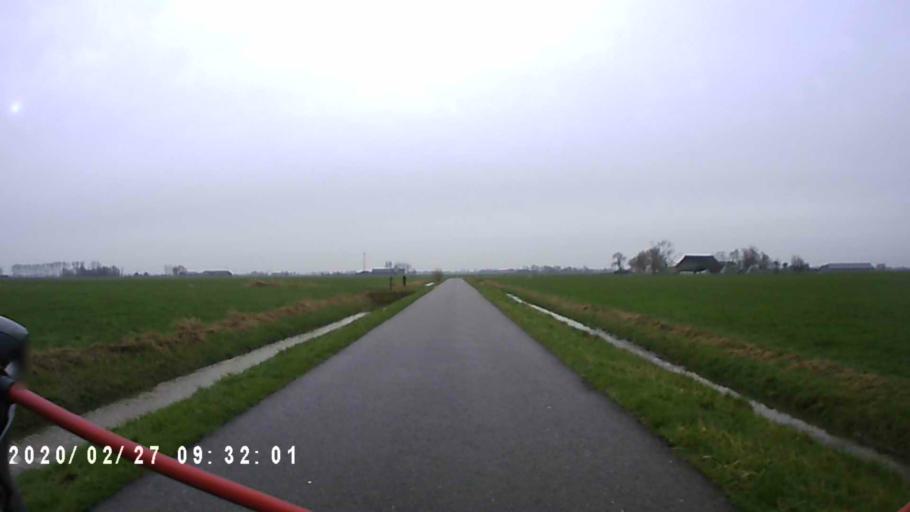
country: NL
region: Groningen
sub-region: Gemeente Zuidhorn
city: Aduard
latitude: 53.2921
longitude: 6.4496
